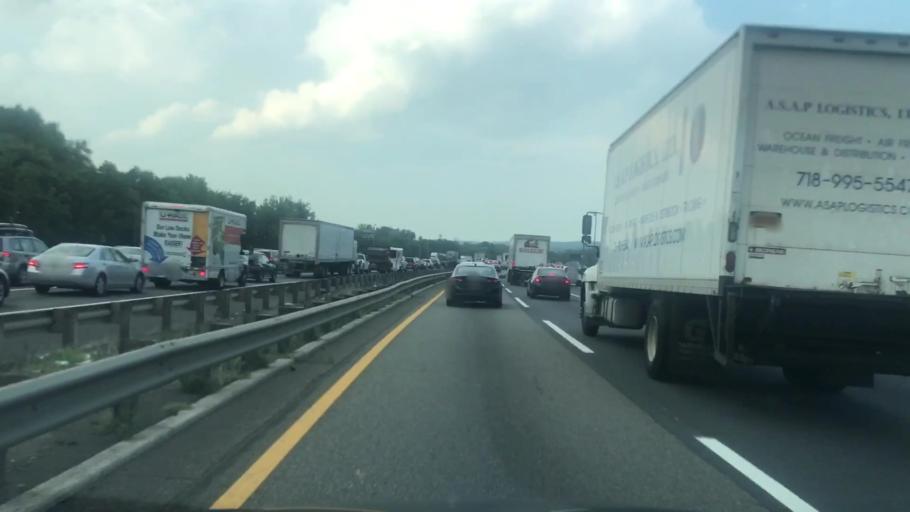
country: US
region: New Jersey
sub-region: Bergen County
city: Leonia
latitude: 40.8722
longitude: -74.0008
